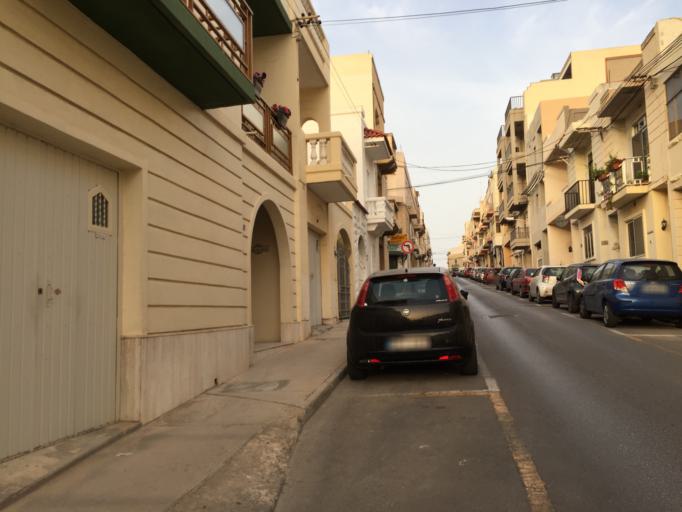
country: MT
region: Il-Fgura
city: Fgura
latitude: 35.8745
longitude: 14.5175
